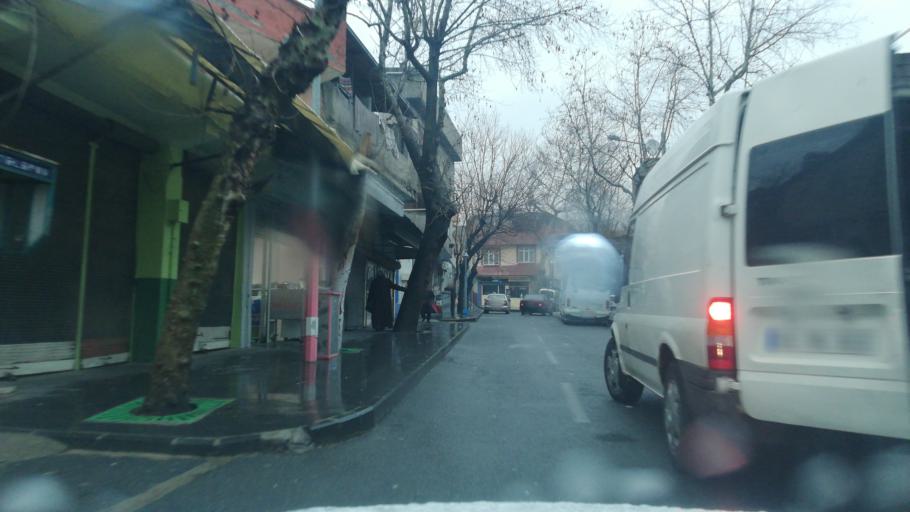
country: TR
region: Kahramanmaras
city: Kahramanmaras
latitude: 37.5817
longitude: 36.9399
